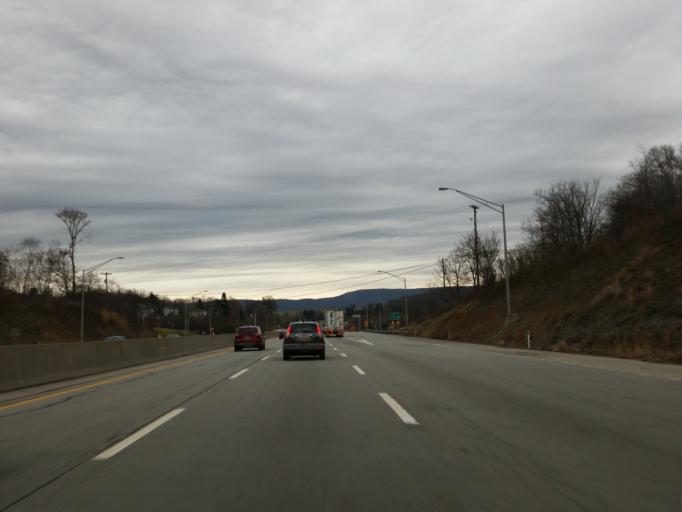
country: US
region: Pennsylvania
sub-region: Fayette County
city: Bear Rocks
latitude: 40.1115
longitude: -79.3866
